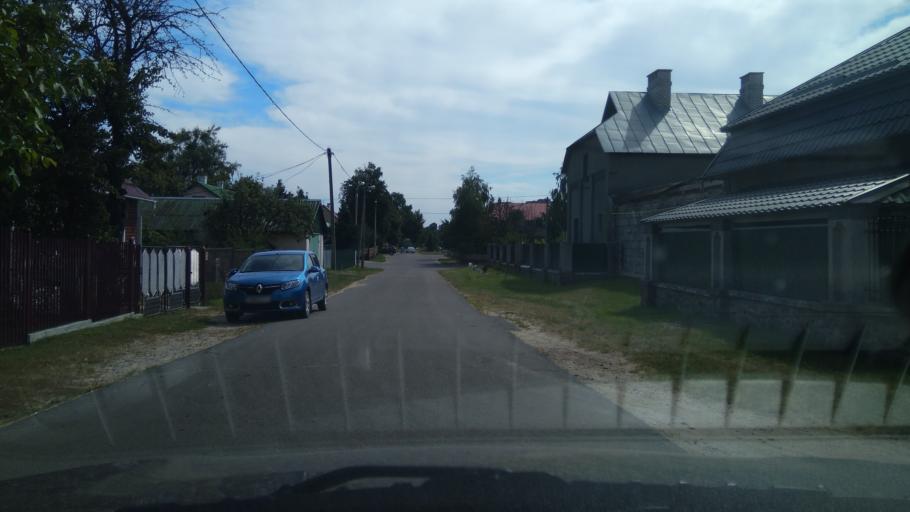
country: BY
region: Brest
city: Ivatsevichy
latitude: 52.7139
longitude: 25.3401
